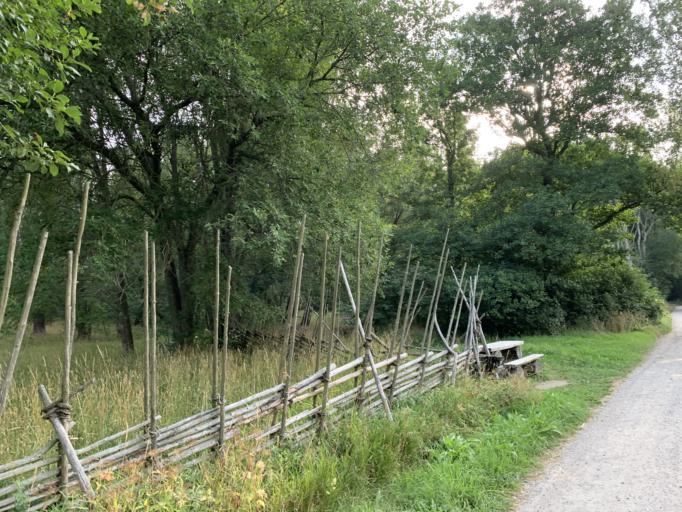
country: SE
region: Stockholm
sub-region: Solna Kommun
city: Rasunda
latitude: 59.3943
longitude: 17.9759
